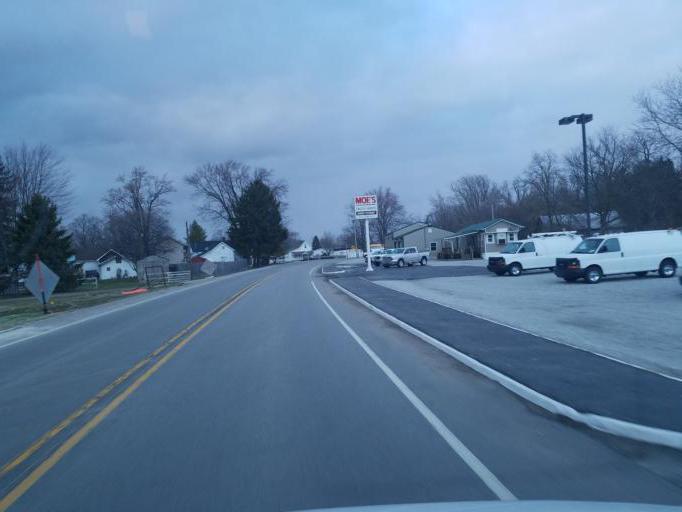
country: US
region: Indiana
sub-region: Henry County
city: Knightstown
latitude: 39.8360
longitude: -85.4339
